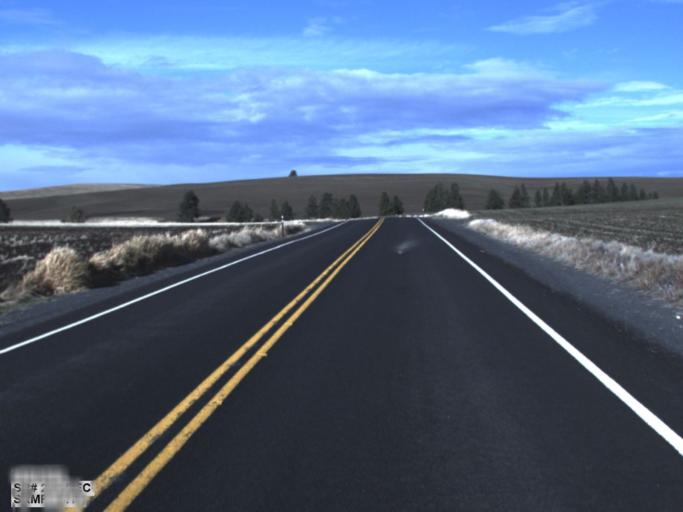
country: US
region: Washington
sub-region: Whitman County
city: Pullman
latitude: 46.9257
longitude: -117.1083
